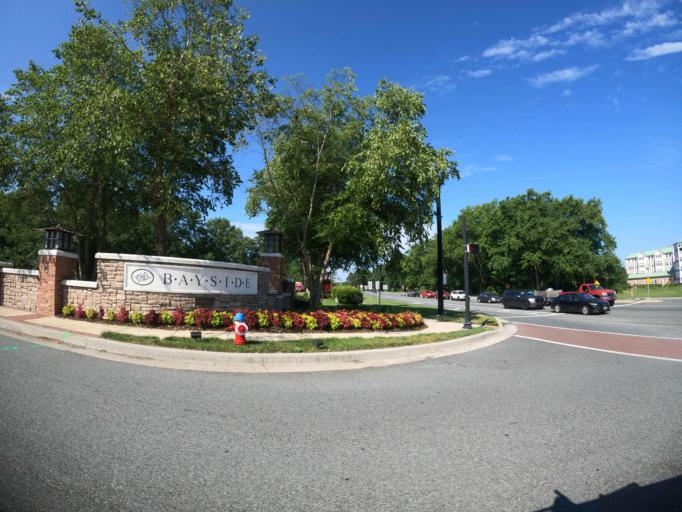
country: US
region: Delaware
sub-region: Sussex County
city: Ocean View
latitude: 38.4696
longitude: -75.1158
